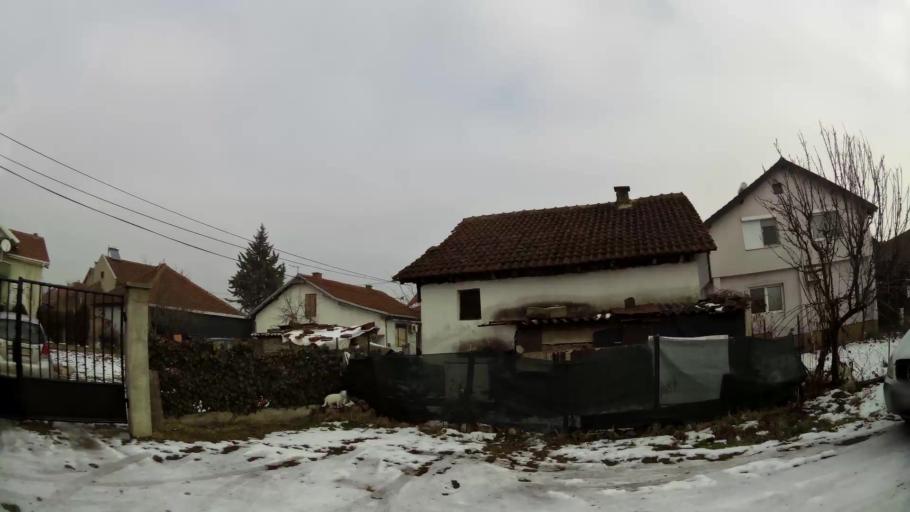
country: MK
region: Ilinden
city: Ilinden
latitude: 41.9931
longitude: 21.5827
